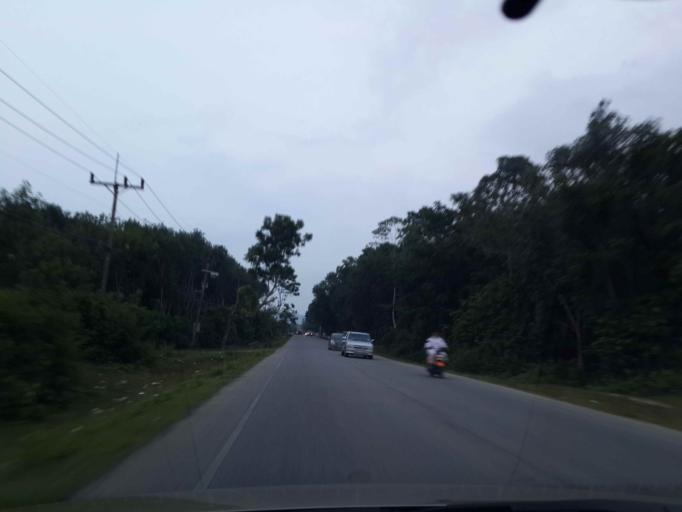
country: TH
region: Narathiwat
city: Rueso
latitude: 6.3626
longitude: 101.5015
